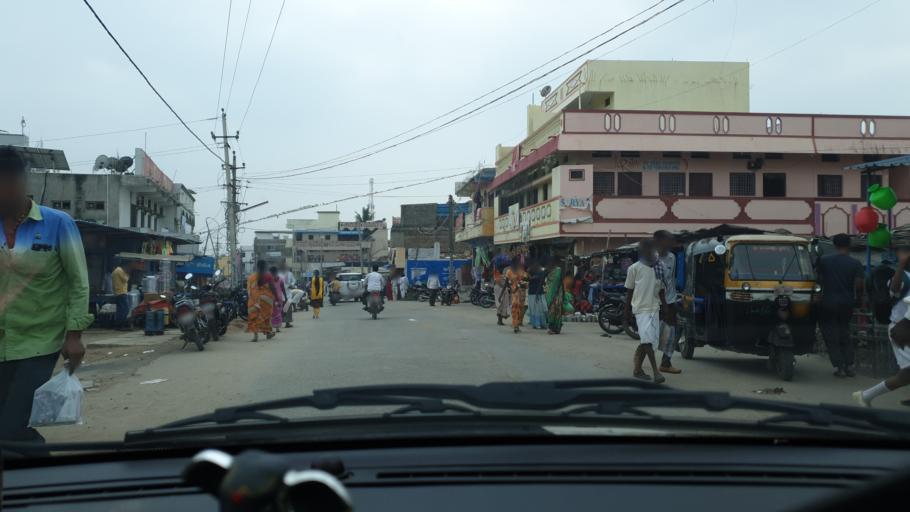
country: IN
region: Karnataka
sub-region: Yadgir
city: Gurmatkal
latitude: 16.8698
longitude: 77.3911
